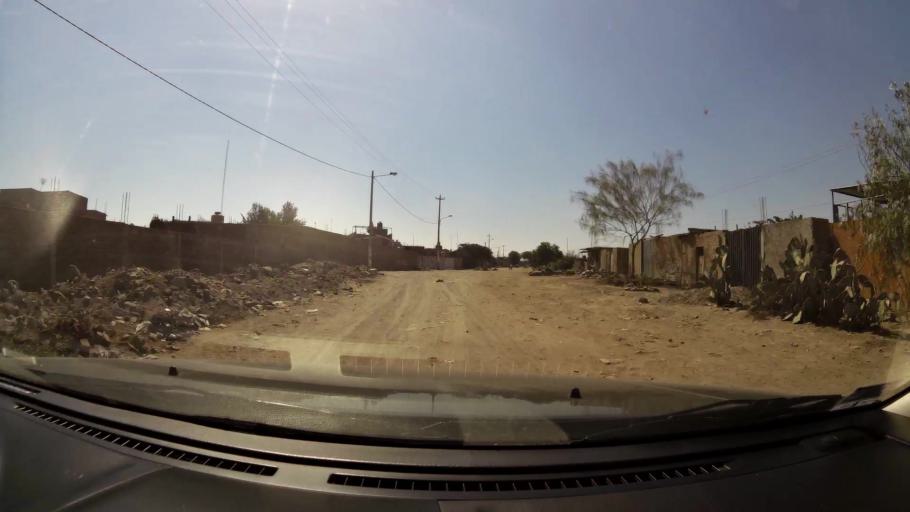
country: PE
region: Ica
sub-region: Provincia de Ica
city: La Tinguina
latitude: -14.0441
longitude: -75.6951
